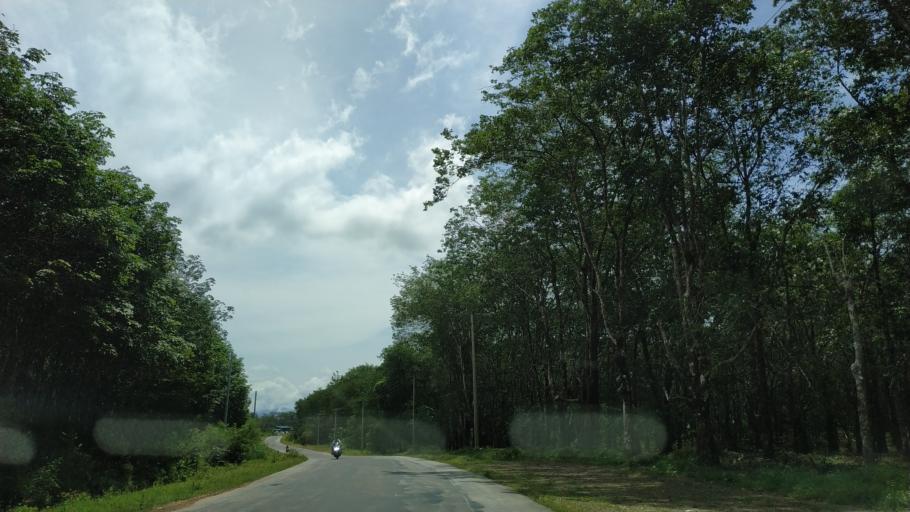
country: MM
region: Tanintharyi
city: Dawei
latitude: 14.1213
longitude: 98.1369
